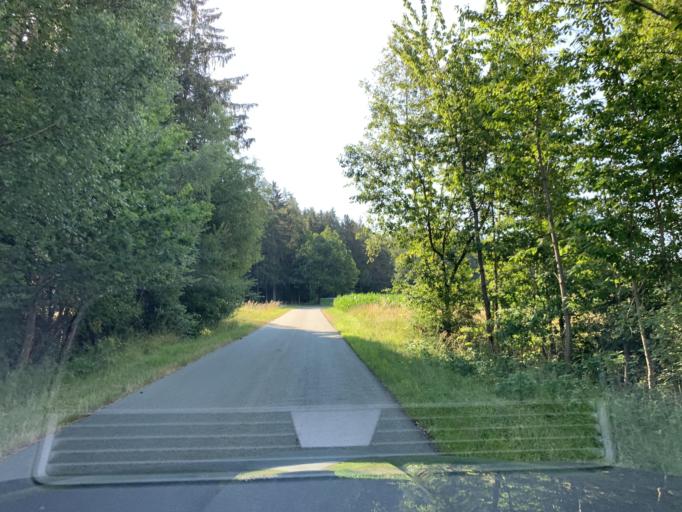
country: DE
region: Bavaria
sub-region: Upper Palatinate
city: Dieterskirchen
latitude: 49.4123
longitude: 12.4324
